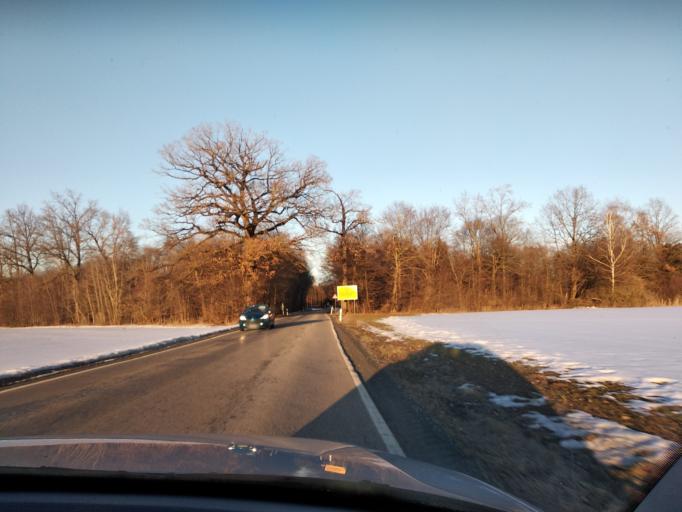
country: DE
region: Bavaria
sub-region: Upper Bavaria
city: Grafing bei Munchen
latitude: 48.0573
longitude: 11.9498
